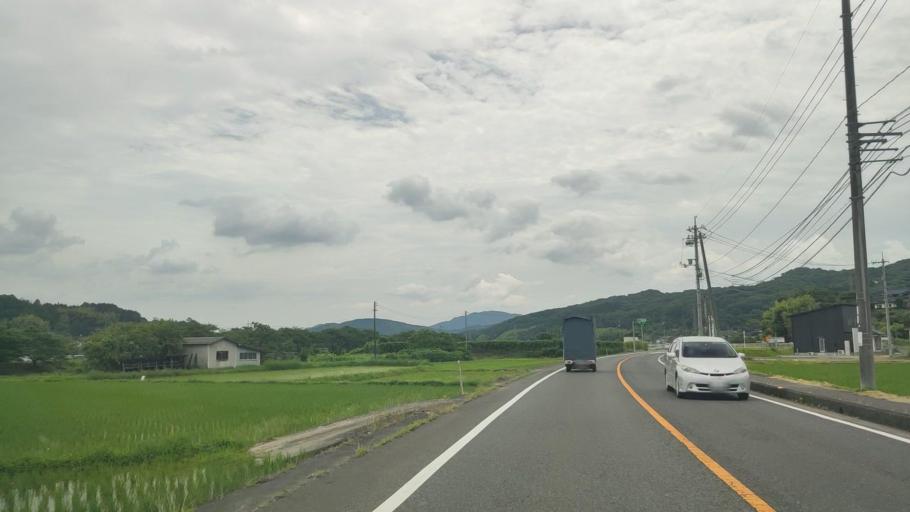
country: JP
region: Okayama
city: Tsuyama
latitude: 35.0570
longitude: 133.9074
